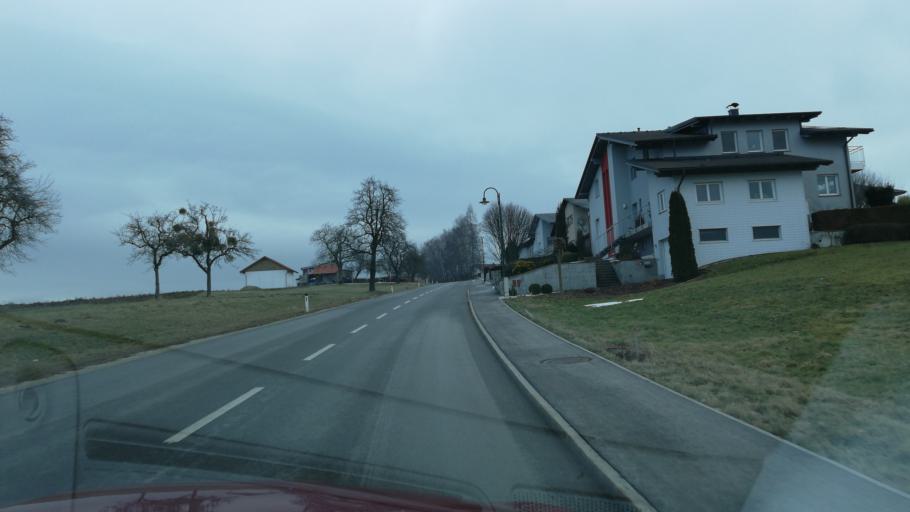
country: AT
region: Upper Austria
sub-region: Wels-Land
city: Bachmanning
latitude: 48.1858
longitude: 13.7496
